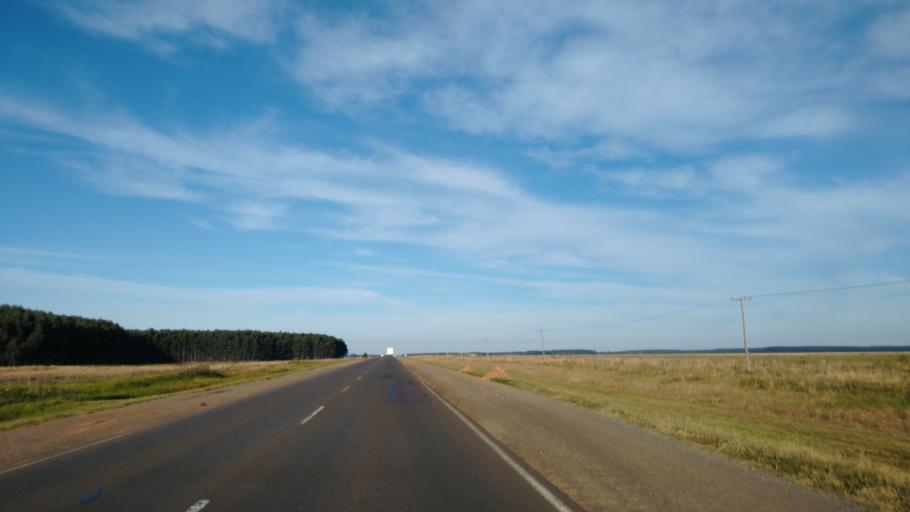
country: AR
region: Corrientes
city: Yapeyu
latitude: -29.3062
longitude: -56.7773
